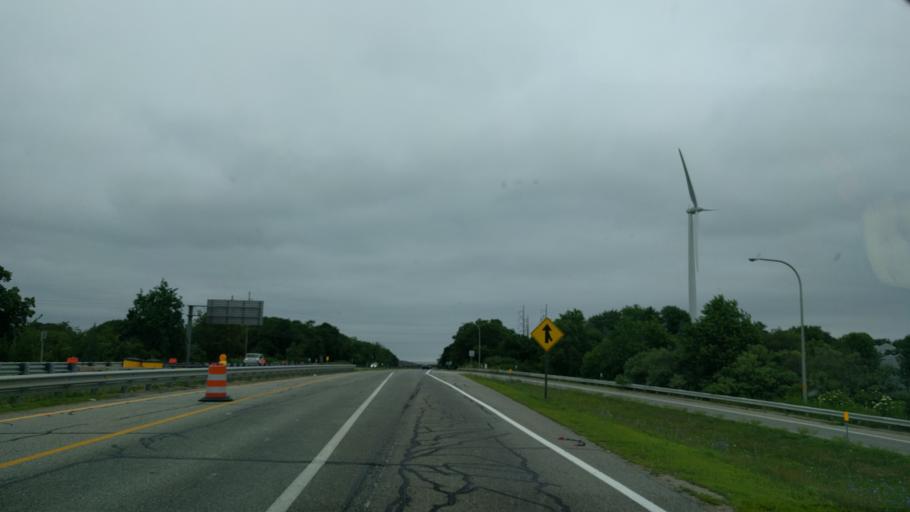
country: US
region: Rhode Island
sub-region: Newport County
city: Portsmouth
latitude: 41.6111
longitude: -71.2541
